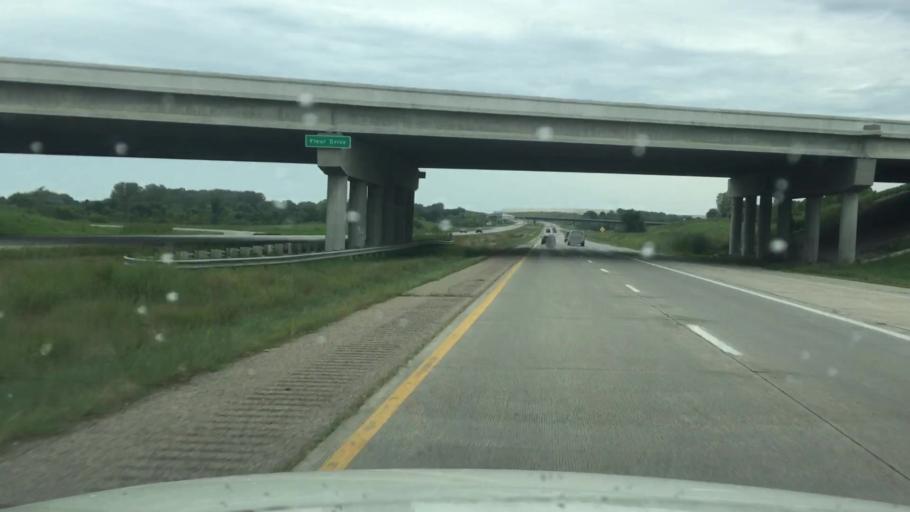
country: US
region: Iowa
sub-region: Warren County
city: Norwalk
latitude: 41.5075
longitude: -93.6444
